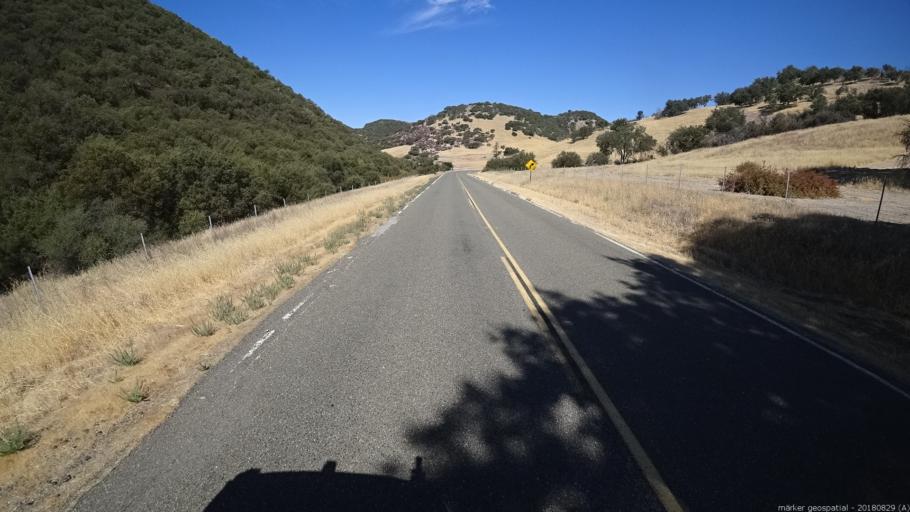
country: US
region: California
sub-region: San Luis Obispo County
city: Lake Nacimiento
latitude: 35.8572
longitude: -121.0603
